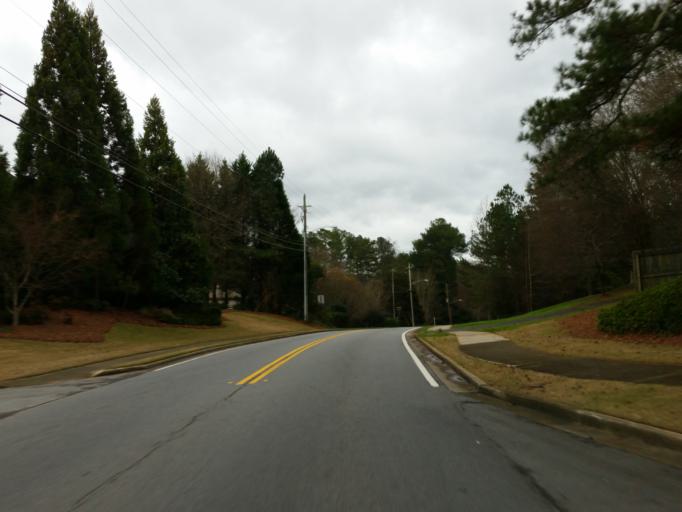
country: US
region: Georgia
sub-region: Cherokee County
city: Woodstock
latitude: 34.0367
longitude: -84.4805
